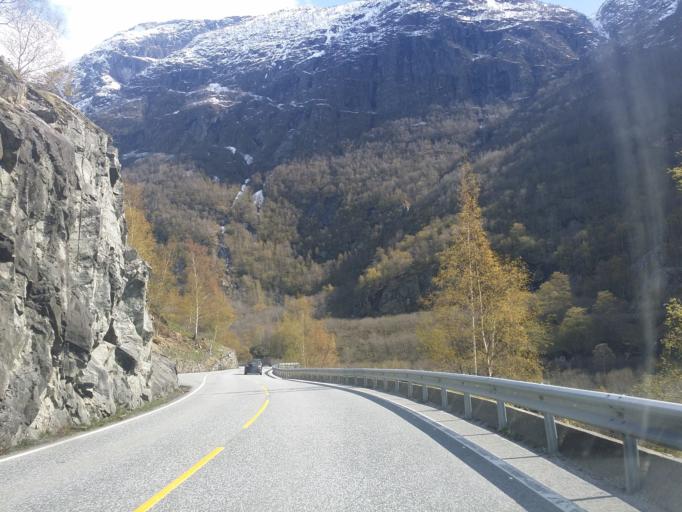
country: NO
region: Hordaland
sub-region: Eidfjord
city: Eidfjord
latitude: 60.4182
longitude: 7.1432
